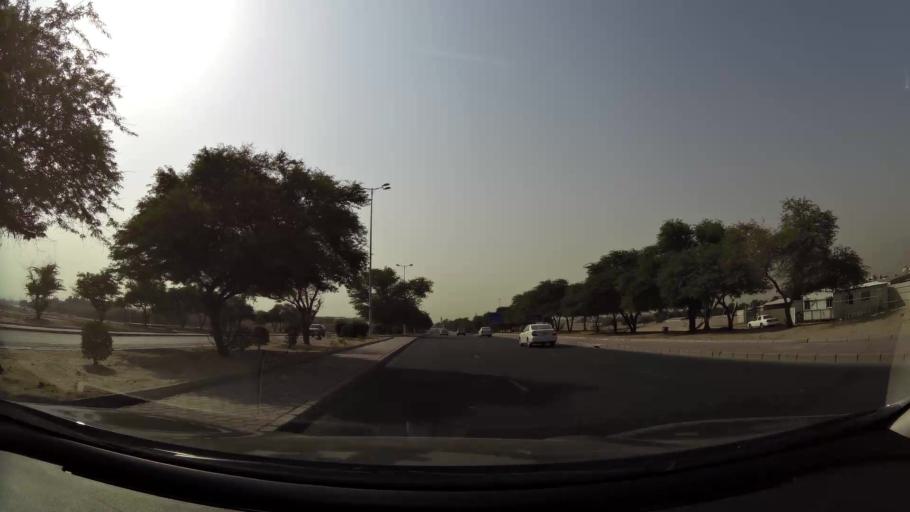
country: KW
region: Al Asimah
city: Ar Rabiyah
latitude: 29.2918
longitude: 47.8319
